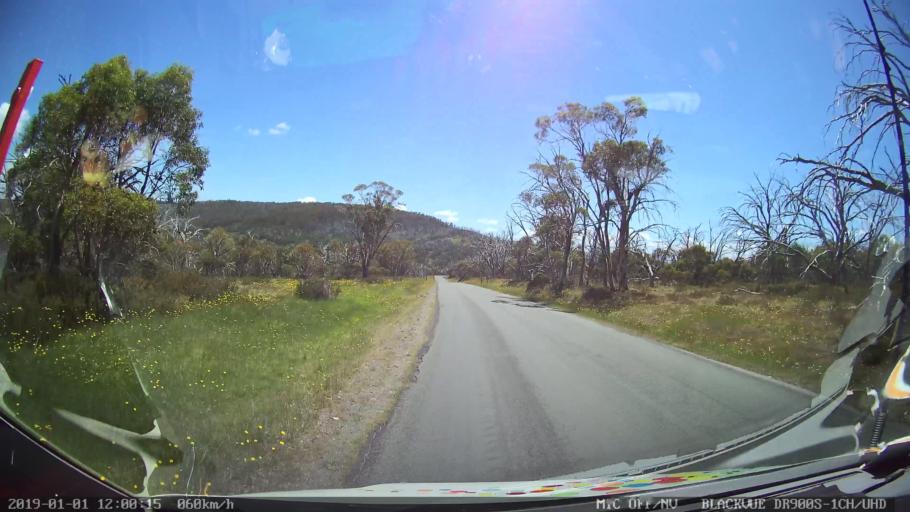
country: AU
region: New South Wales
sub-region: Snowy River
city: Jindabyne
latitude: -35.8864
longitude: 148.4585
